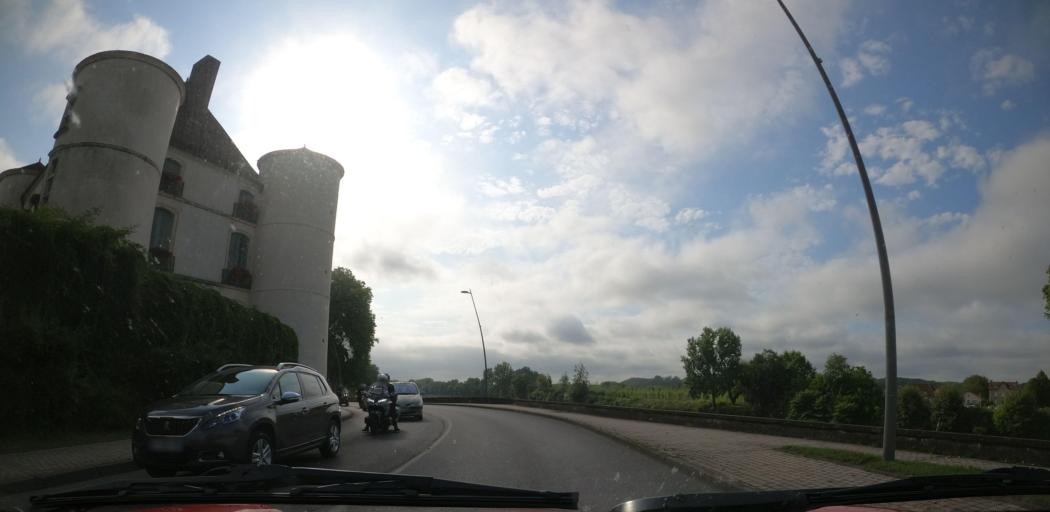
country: FR
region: Aquitaine
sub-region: Departement des Landes
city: Peyrehorade
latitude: 43.5438
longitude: -1.1048
